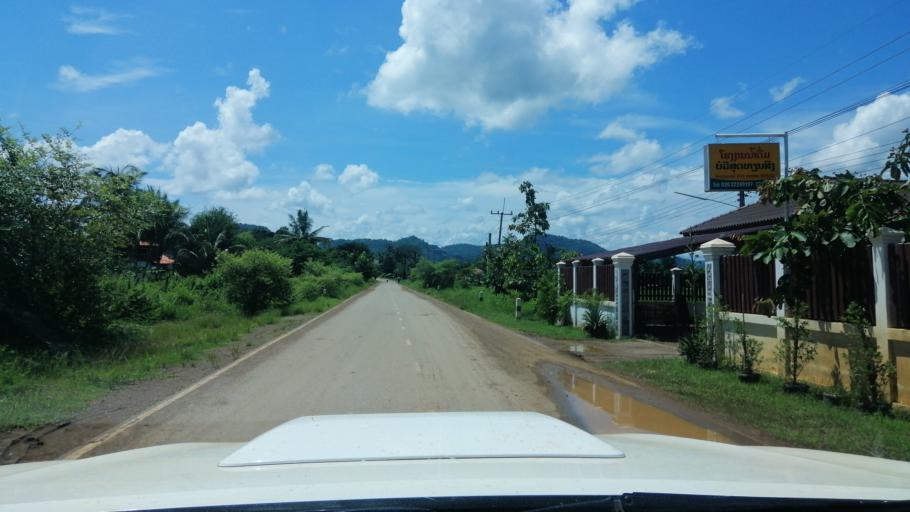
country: TH
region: Uttaradit
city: Ban Khok
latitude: 18.1355
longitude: 101.2747
